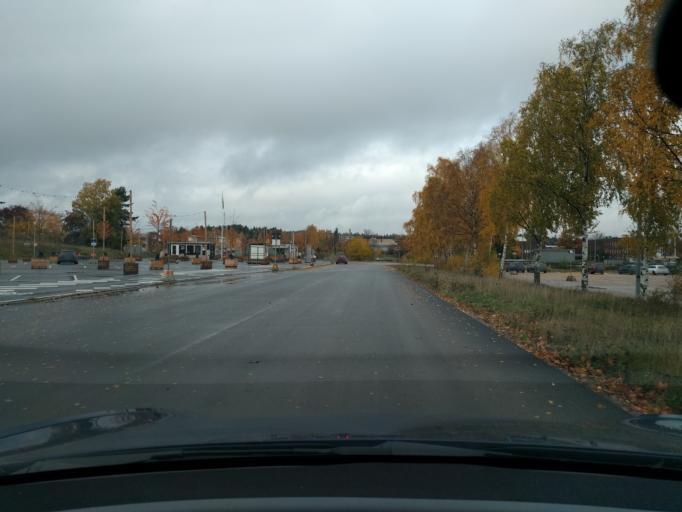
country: SE
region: Stockholm
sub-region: Taby Kommun
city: Taby
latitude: 59.4457
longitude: 18.0855
